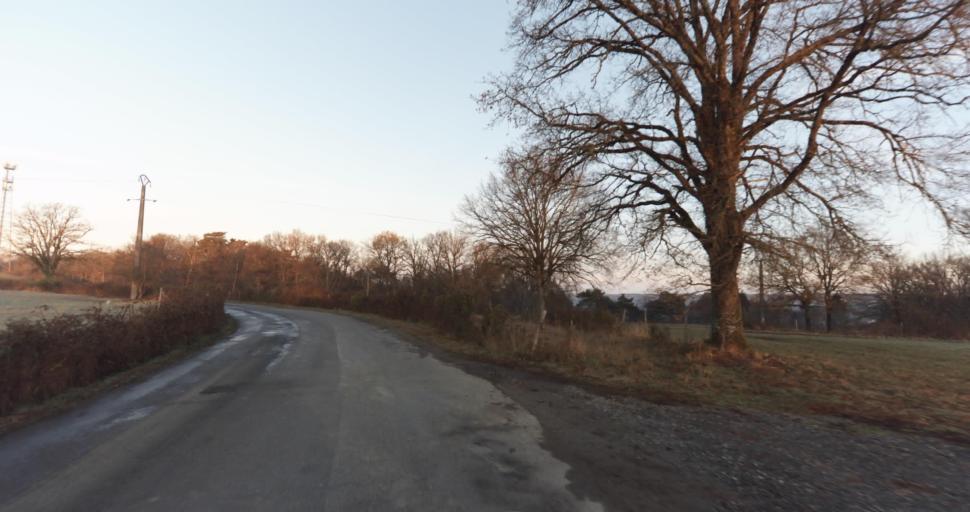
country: FR
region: Limousin
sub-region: Departement de la Haute-Vienne
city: Aixe-sur-Vienne
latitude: 45.8150
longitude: 1.1657
